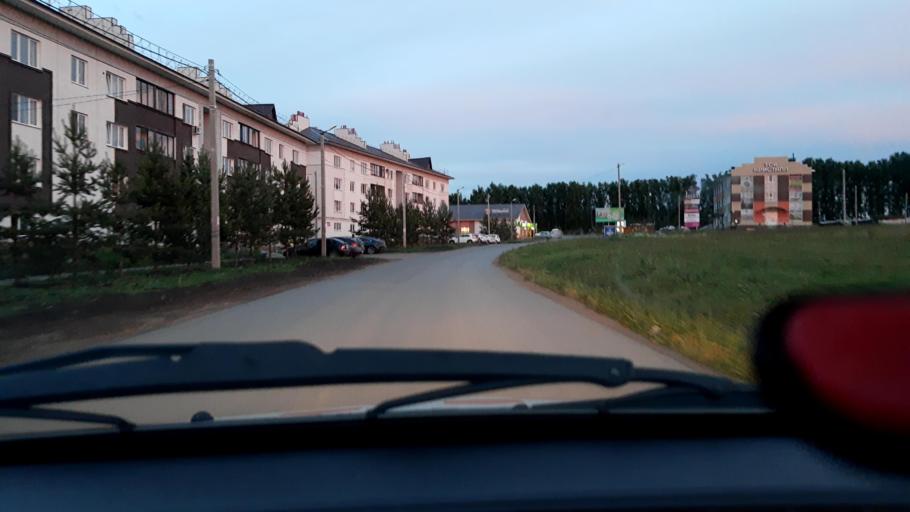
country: RU
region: Bashkortostan
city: Avdon
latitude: 54.4770
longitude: 55.8771
